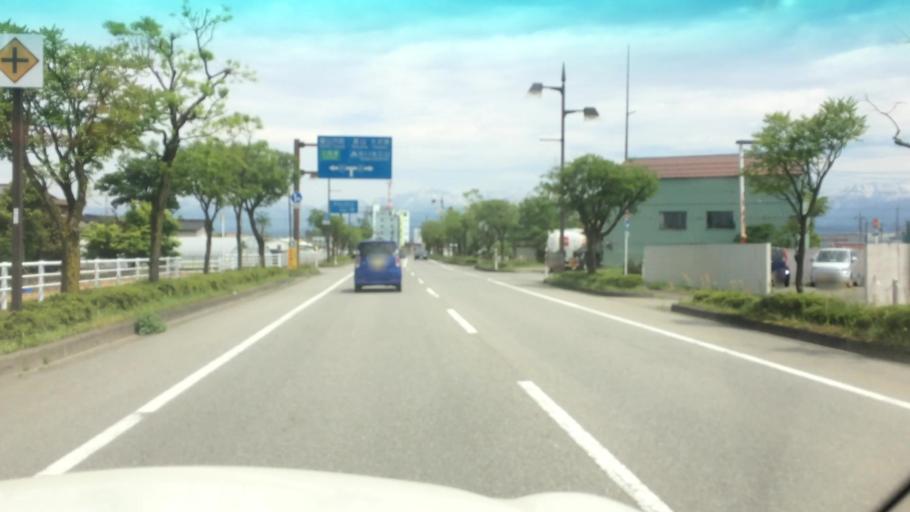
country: JP
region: Toyama
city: Toyama-shi
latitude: 36.6432
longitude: 137.2073
